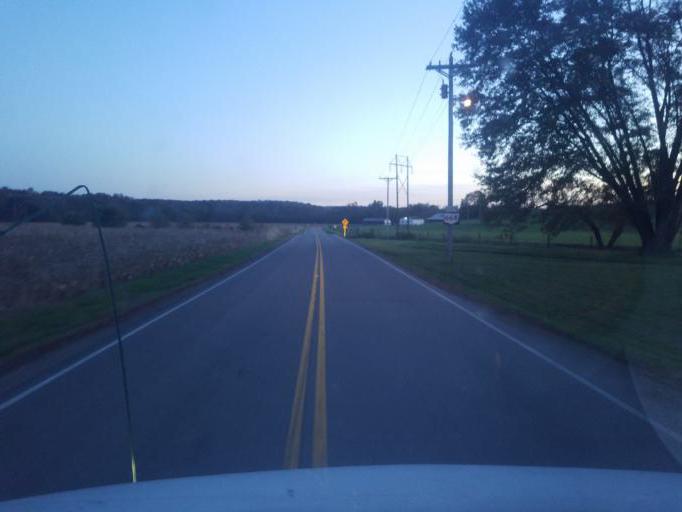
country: US
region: Ohio
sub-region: Perry County
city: Somerset
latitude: 39.8912
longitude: -82.2438
